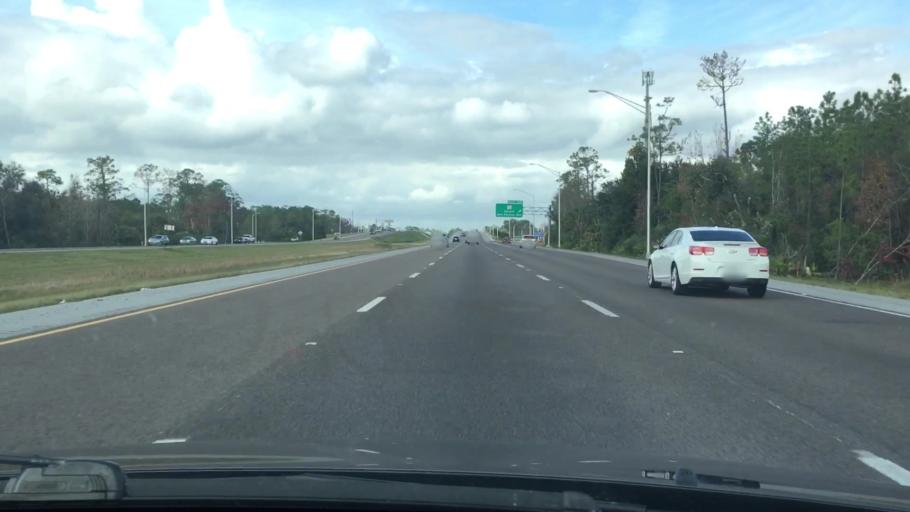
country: US
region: Florida
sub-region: Volusia County
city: Glencoe
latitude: 29.0079
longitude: -80.9844
